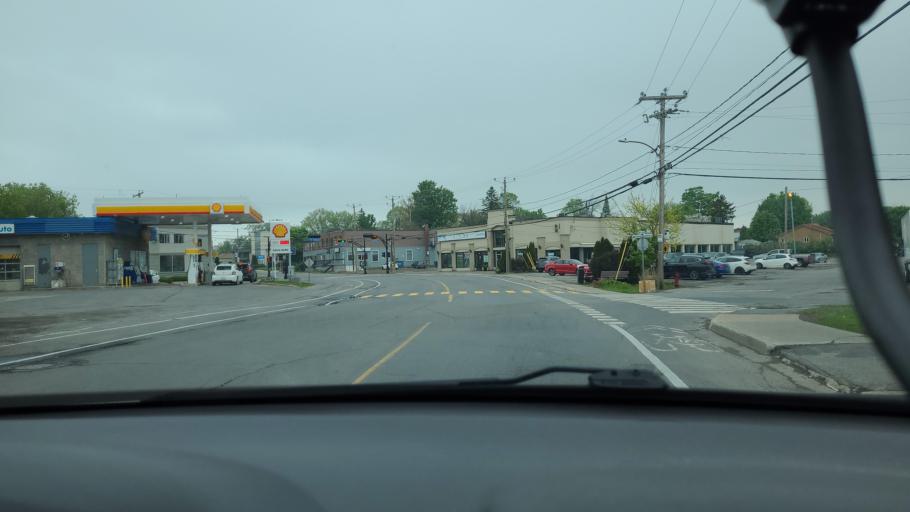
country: CA
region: Quebec
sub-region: Monteregie
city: L'Ile-Perrot
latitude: 45.3953
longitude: -73.9577
